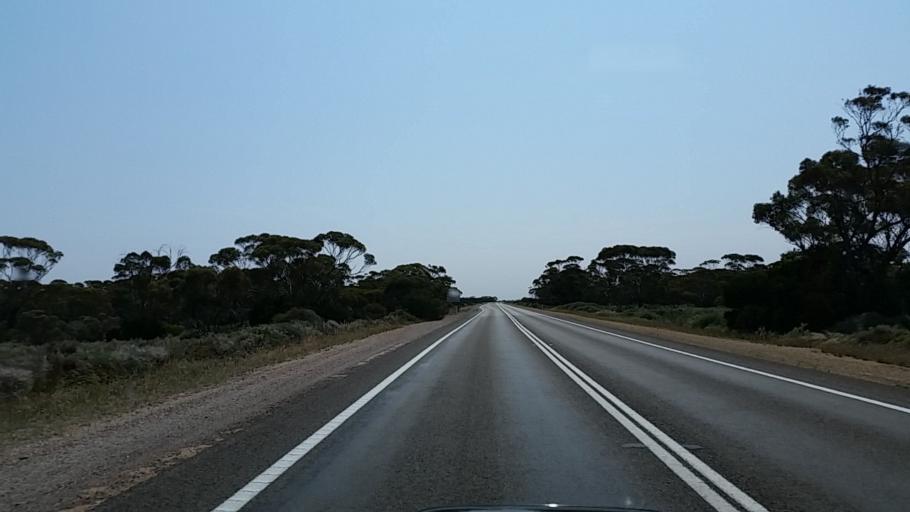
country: AU
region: South Australia
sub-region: Port Pirie City and Dists
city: Port Pirie
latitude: -32.9851
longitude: 137.9855
